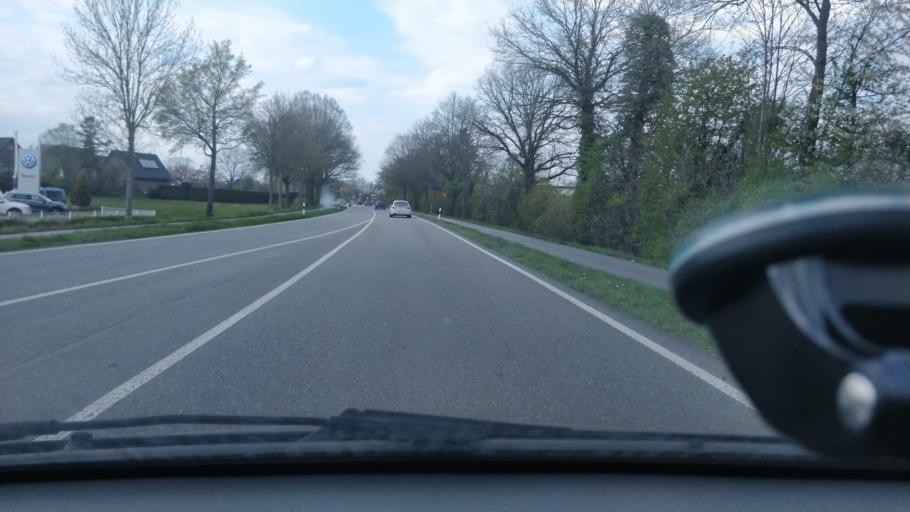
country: DE
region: North Rhine-Westphalia
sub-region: Regierungsbezirk Dusseldorf
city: Hamminkeln
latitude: 51.7352
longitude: 6.6002
